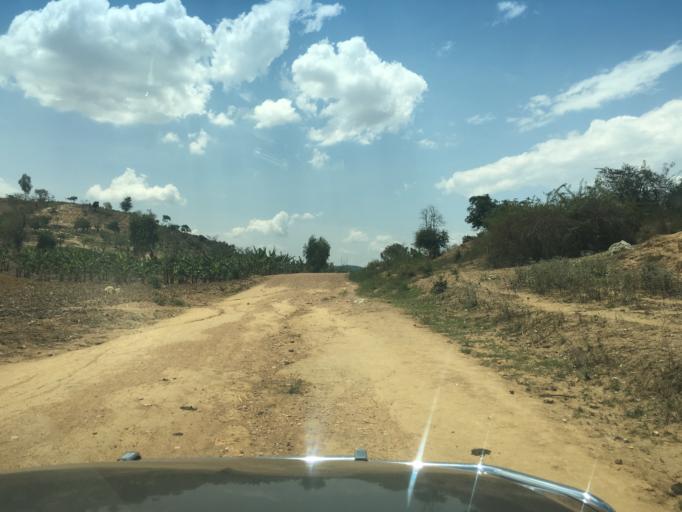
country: RW
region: Eastern Province
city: Kibungo
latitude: -2.1232
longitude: 30.8532
